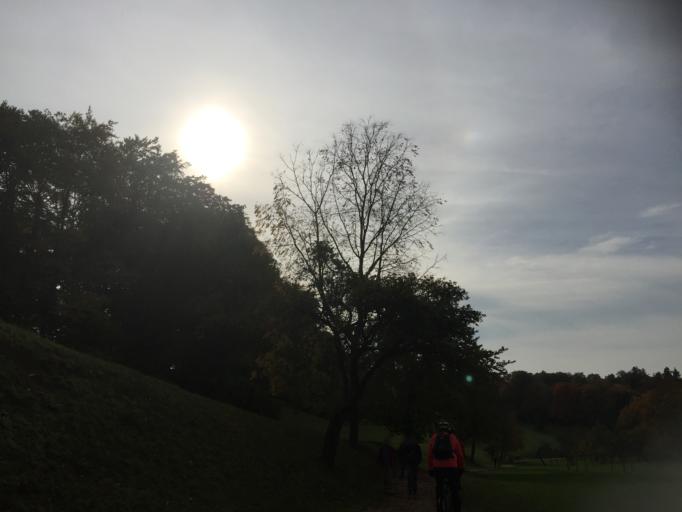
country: DE
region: Hesse
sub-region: Regierungsbezirk Darmstadt
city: Bensheim
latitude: 49.7014
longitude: 8.6430
